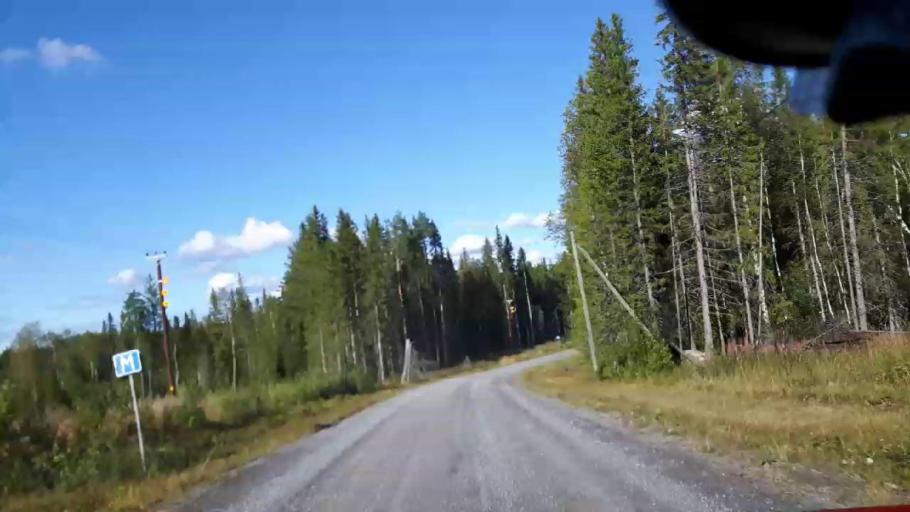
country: SE
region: Jaemtland
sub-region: Ragunda Kommun
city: Hammarstrand
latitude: 63.5130
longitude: 16.0498
